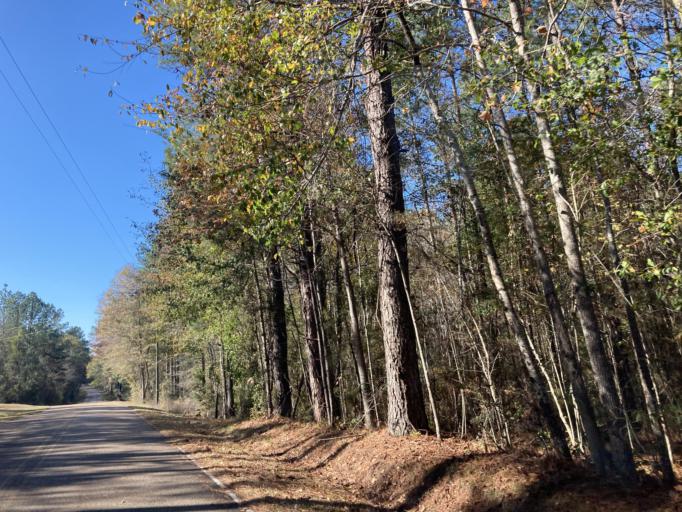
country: US
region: Mississippi
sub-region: Lamar County
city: Sumrall
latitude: 31.2555
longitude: -89.5421
